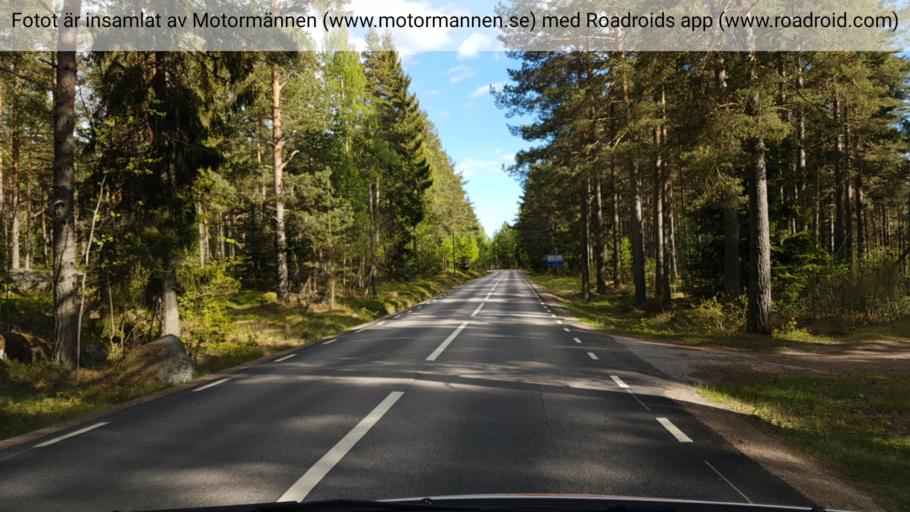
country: SE
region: Kalmar
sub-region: Vasterviks Kommun
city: Vaestervik
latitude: 57.9117
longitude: 16.6418
